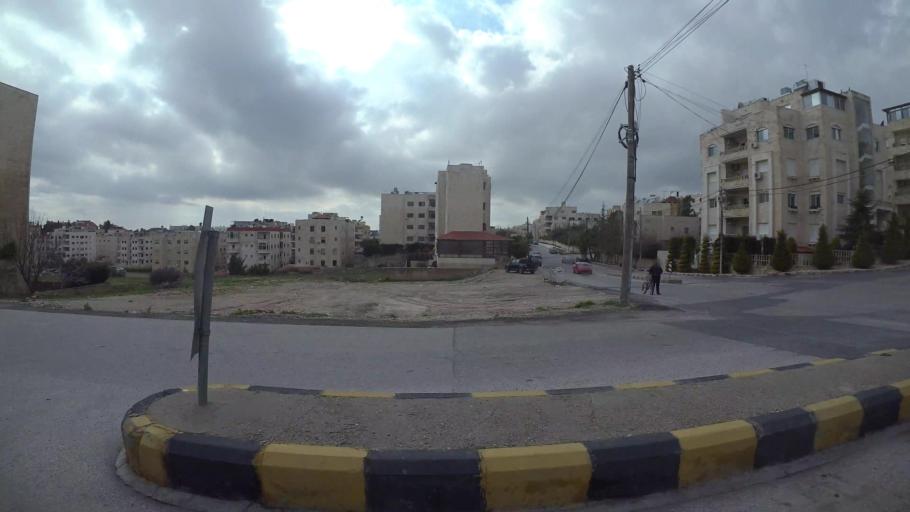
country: JO
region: Amman
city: Wadi as Sir
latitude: 31.9850
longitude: 35.8441
